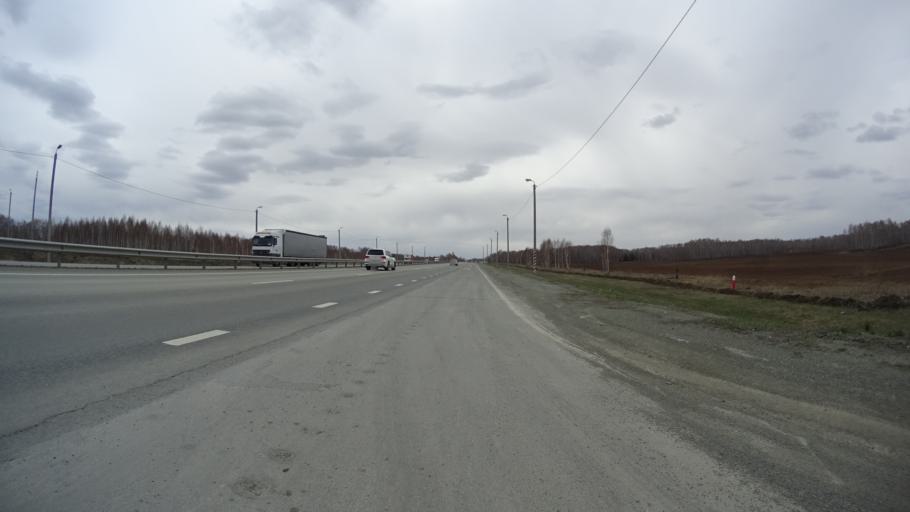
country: RU
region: Chelyabinsk
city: Yemanzhelinka
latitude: 54.8334
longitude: 61.3122
